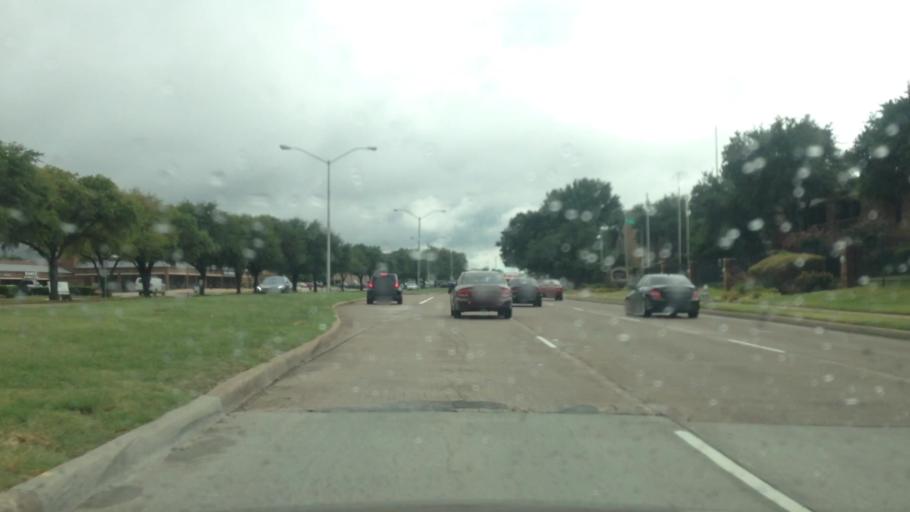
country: US
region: Texas
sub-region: Tarrant County
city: Edgecliff Village
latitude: 32.6704
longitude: -97.4000
